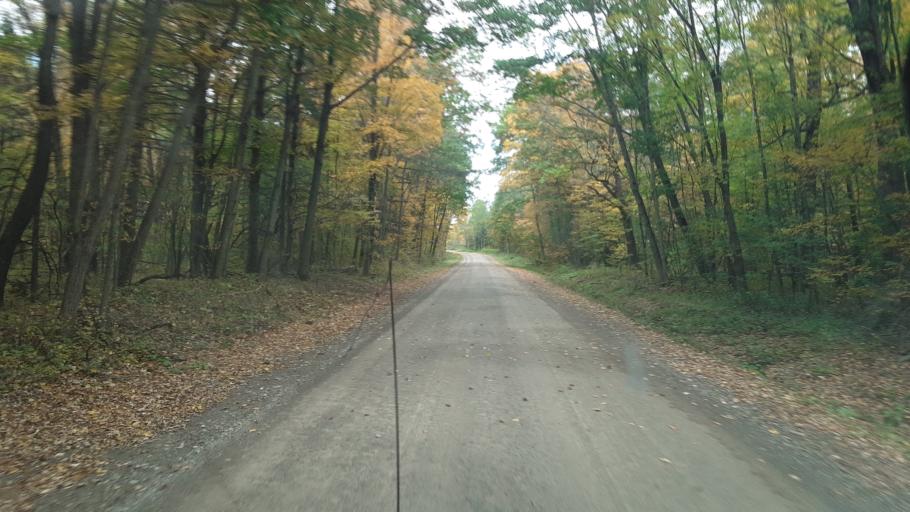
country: US
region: New York
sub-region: Allegany County
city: Alfred
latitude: 42.3740
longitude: -77.8498
